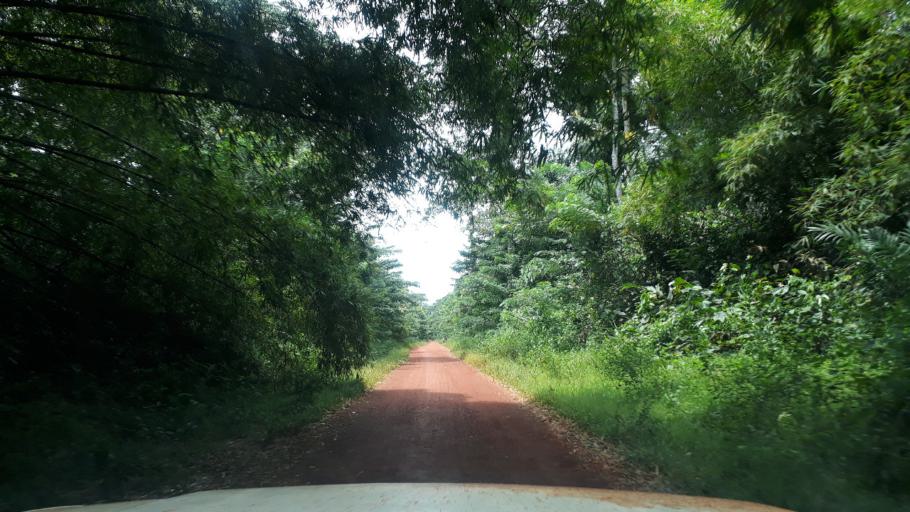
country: CD
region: Eastern Province
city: Aketi
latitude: 2.9326
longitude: 24.0928
